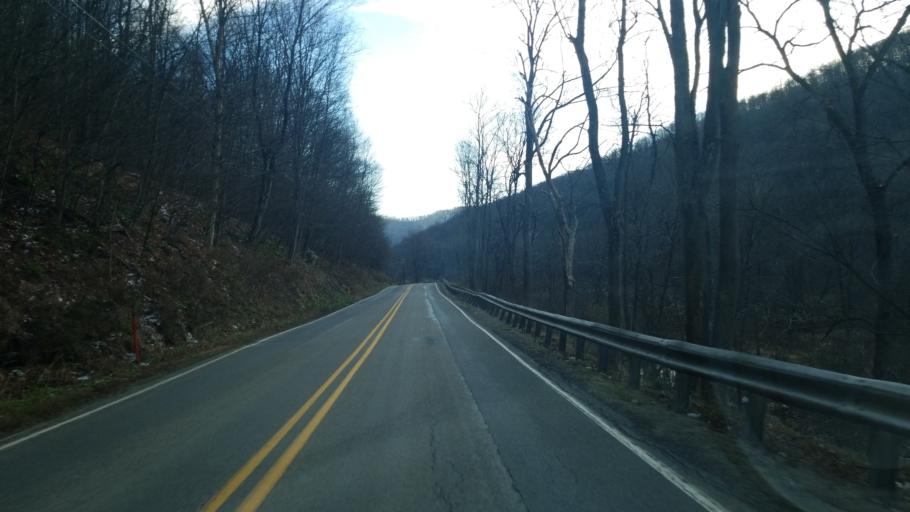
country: US
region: Pennsylvania
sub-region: Potter County
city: Coudersport
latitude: 41.6485
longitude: -78.0856
